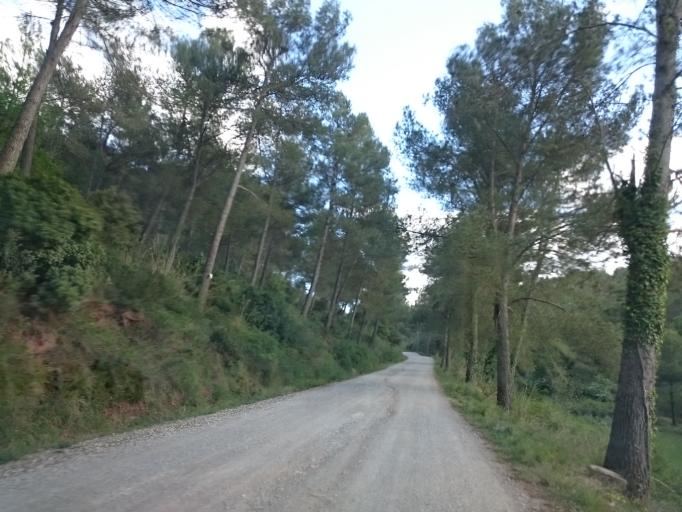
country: ES
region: Catalonia
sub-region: Provincia de Barcelona
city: Begues
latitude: 41.3220
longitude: 1.9217
